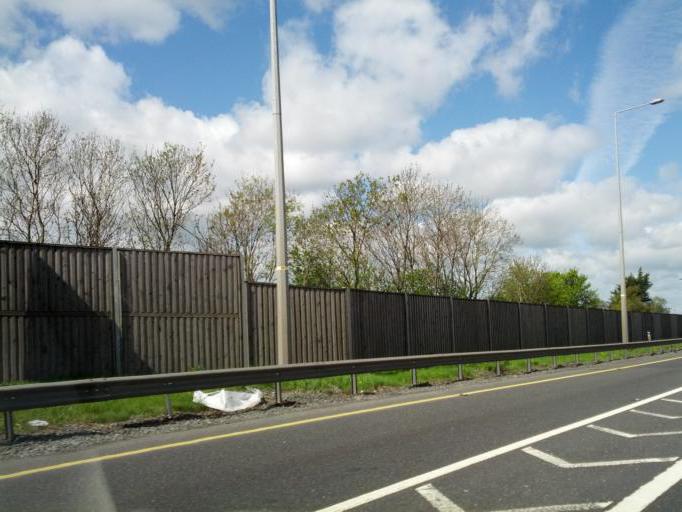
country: IE
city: Cherry Orchard
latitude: 53.3241
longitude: -6.3733
